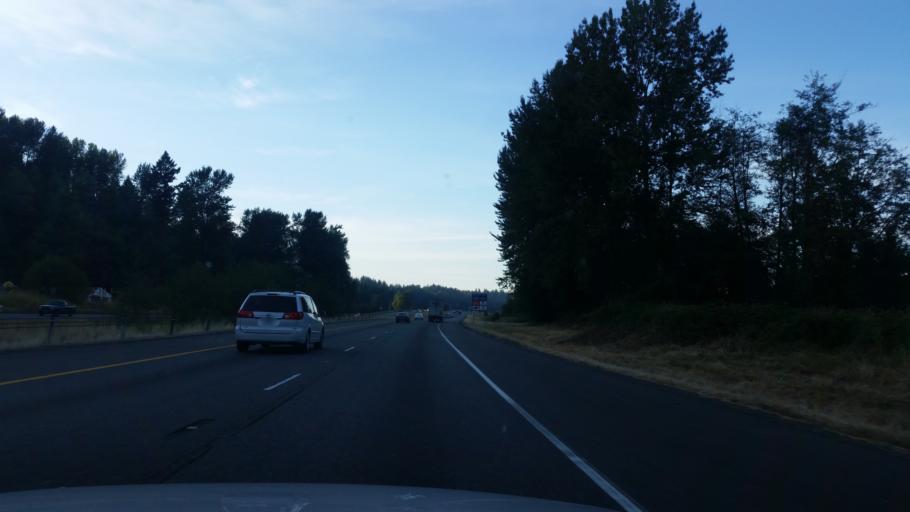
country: US
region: Washington
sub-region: King County
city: Pacific
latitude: 47.2429
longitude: -122.2548
